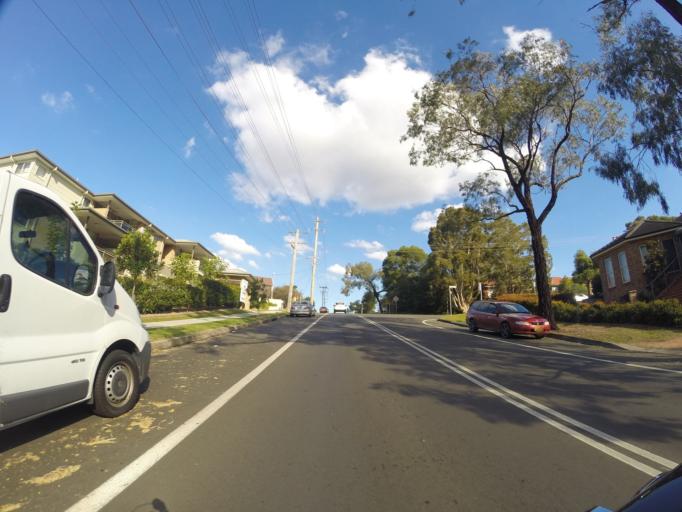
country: AU
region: New South Wales
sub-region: Wollongong
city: Keiraville
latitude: -34.4152
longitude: 150.8702
